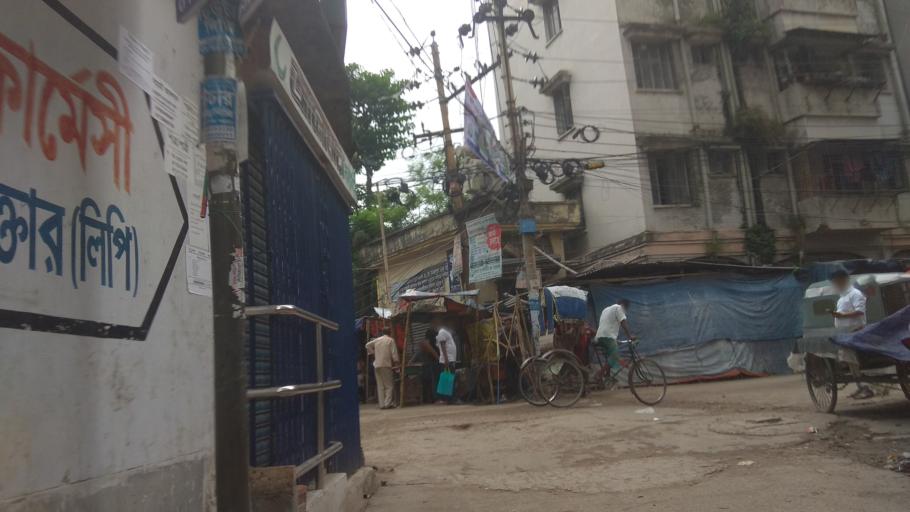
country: BD
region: Dhaka
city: Azimpur
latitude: 23.8016
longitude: 90.3781
